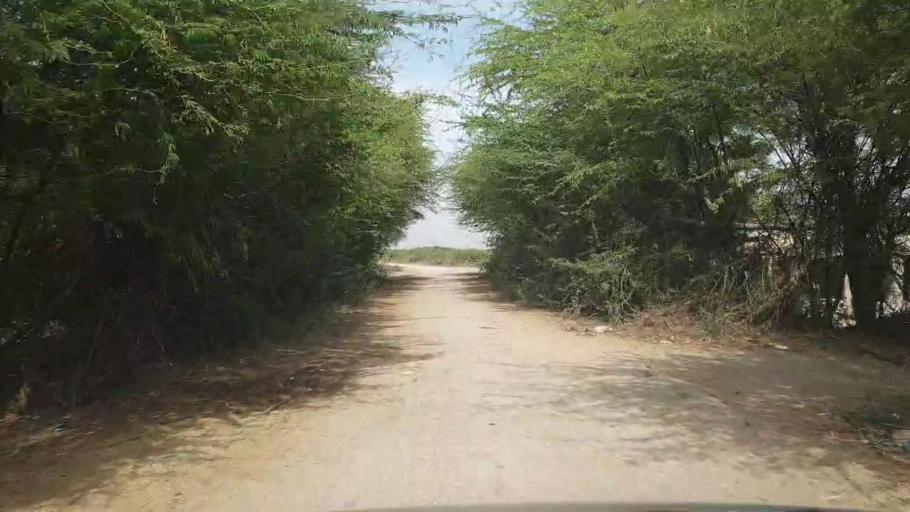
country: PK
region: Sindh
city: Kunri
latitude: 25.2317
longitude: 69.6710
